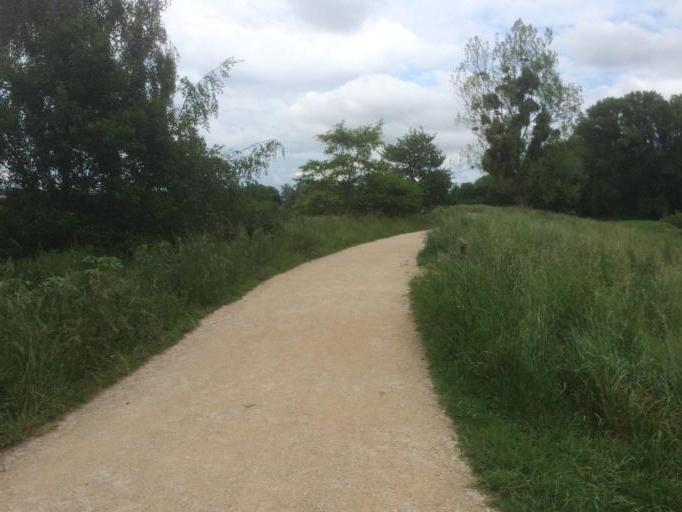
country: FR
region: Ile-de-France
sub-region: Departement de l'Essonne
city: Saulx-les-Chartreux
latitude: 48.6956
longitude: 2.2780
